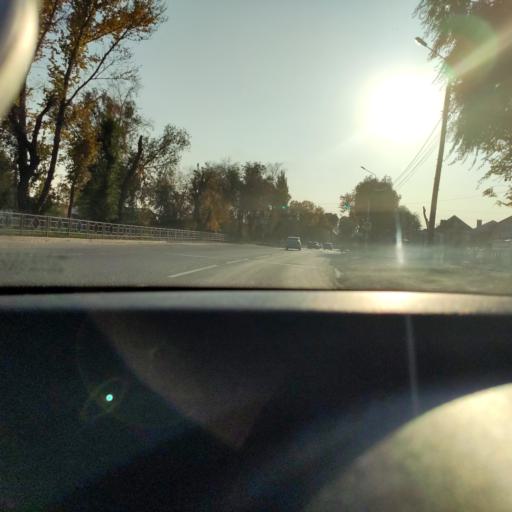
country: RU
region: Samara
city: Smyshlyayevka
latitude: 53.2317
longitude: 50.3063
